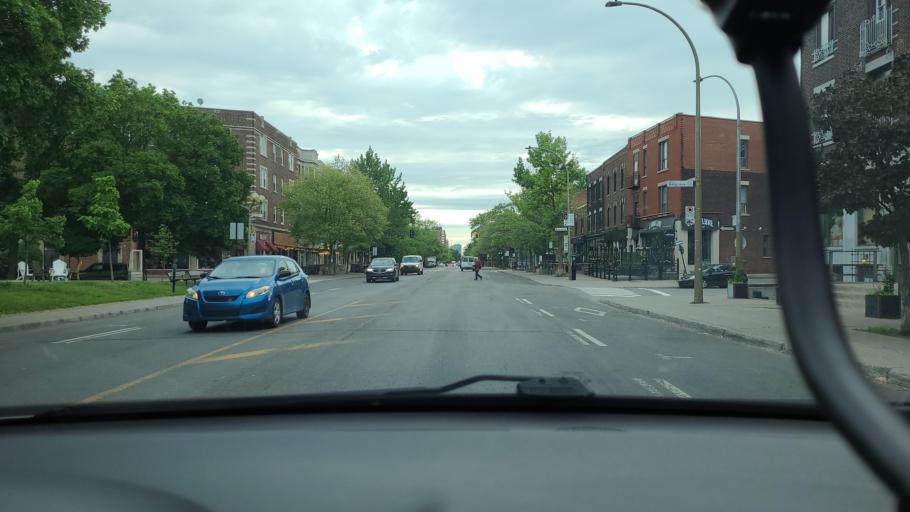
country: CA
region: Quebec
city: Saint-Raymond
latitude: 45.4685
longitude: -73.6200
